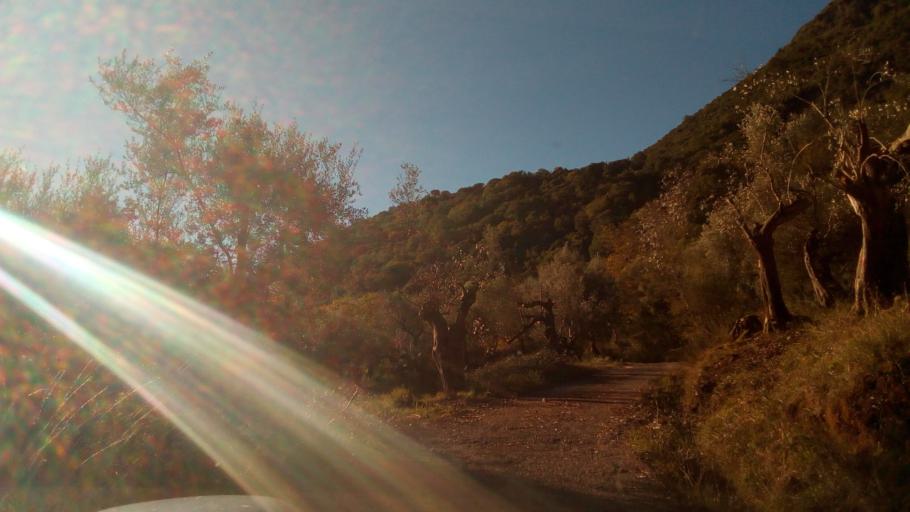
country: GR
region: West Greece
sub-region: Nomos Aitolias kai Akarnanias
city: Nafpaktos
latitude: 38.4631
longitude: 21.8767
